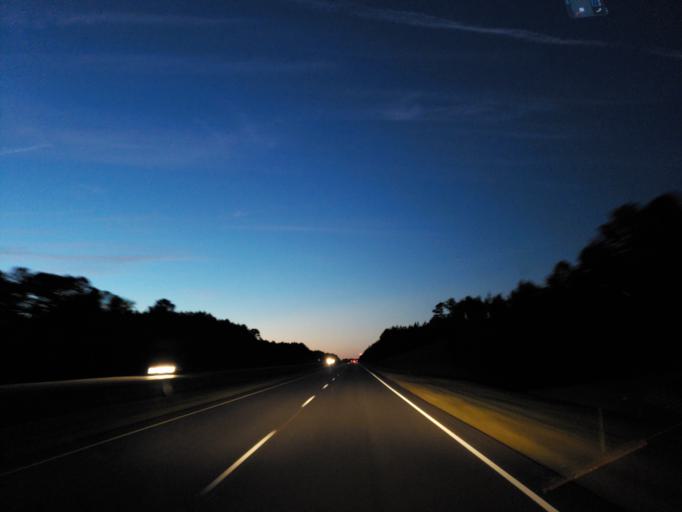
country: US
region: Mississippi
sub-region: Clarke County
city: Quitman
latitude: 32.0785
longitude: -88.6904
